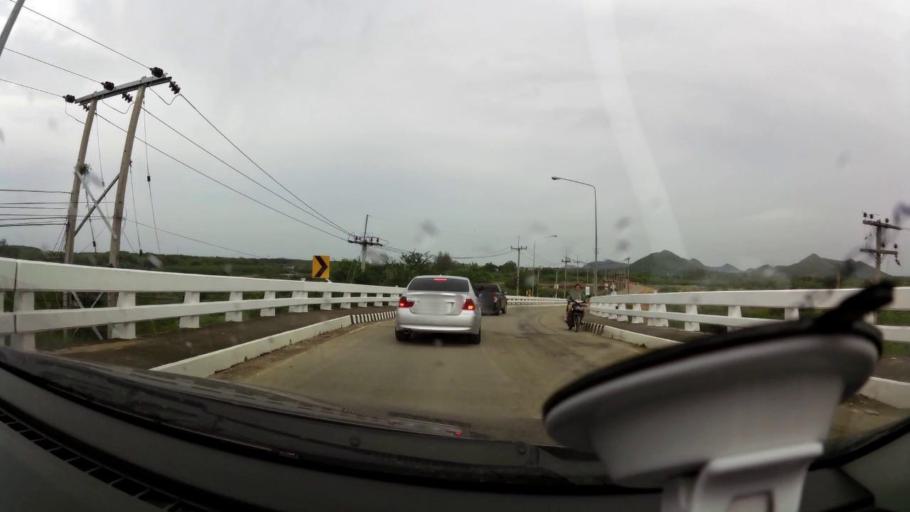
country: TH
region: Prachuap Khiri Khan
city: Pran Buri
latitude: 12.4048
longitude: 99.9669
